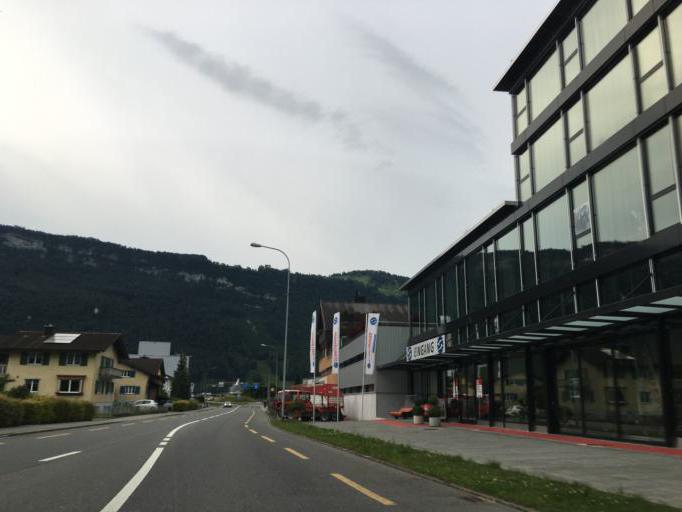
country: CH
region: Nidwalden
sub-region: Nidwalden
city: Stans
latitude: 46.9630
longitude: 8.3854
